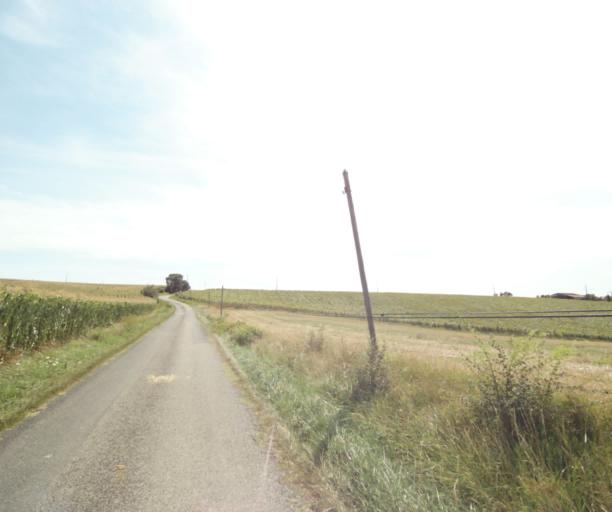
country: FR
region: Midi-Pyrenees
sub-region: Departement de la Haute-Garonne
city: Gaillac-Toulza
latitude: 43.2537
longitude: 1.4205
